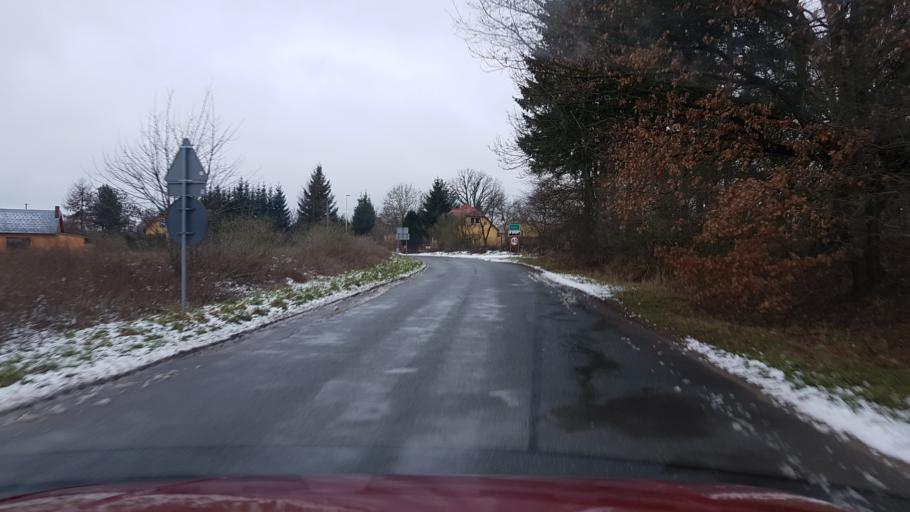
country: PL
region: West Pomeranian Voivodeship
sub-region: Powiat goleniowski
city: Nowogard
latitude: 53.6651
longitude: 15.1880
